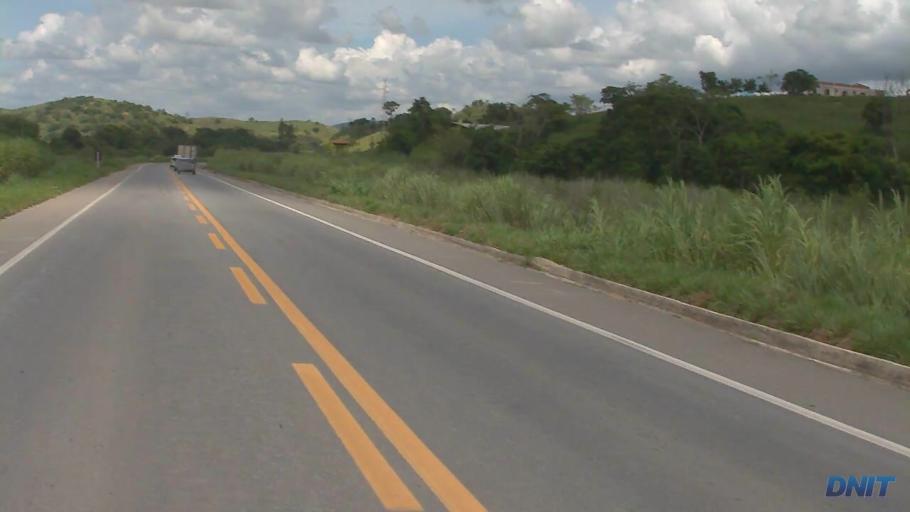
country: BR
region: Minas Gerais
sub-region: Governador Valadares
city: Governador Valadares
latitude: -18.9872
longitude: -42.1101
